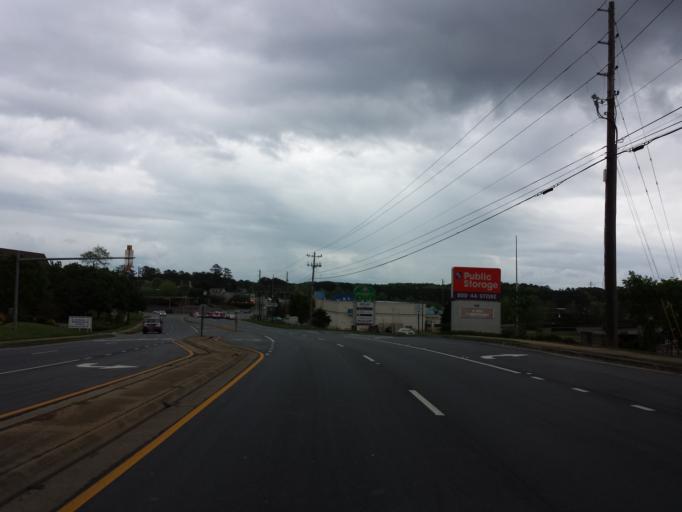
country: US
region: Georgia
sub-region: Cobb County
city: Marietta
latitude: 34.0190
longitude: -84.5313
